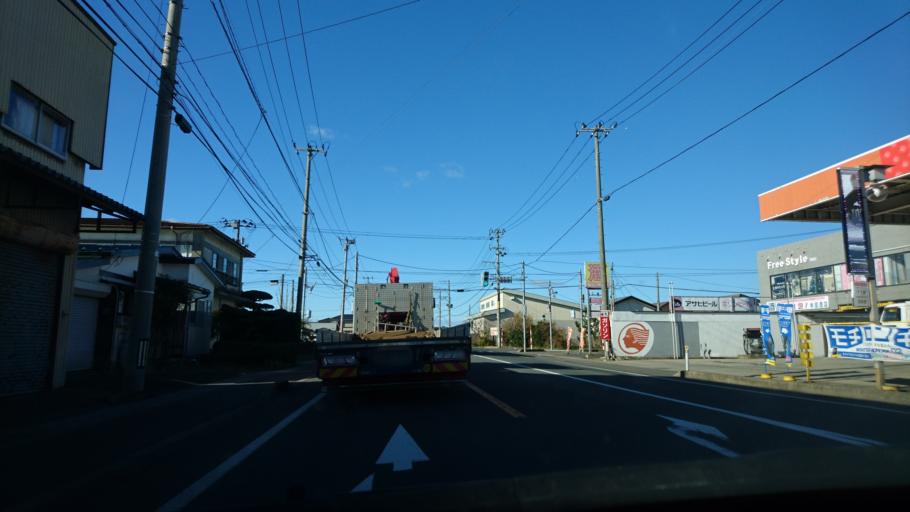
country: JP
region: Akita
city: Akita
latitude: 39.3588
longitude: 140.0772
